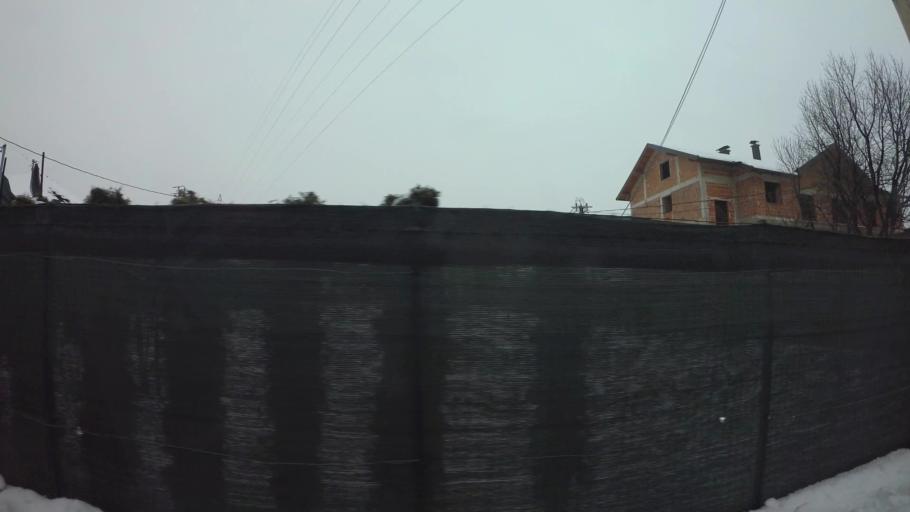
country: BA
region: Federation of Bosnia and Herzegovina
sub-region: Kanton Sarajevo
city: Sarajevo
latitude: 43.8349
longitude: 18.2829
